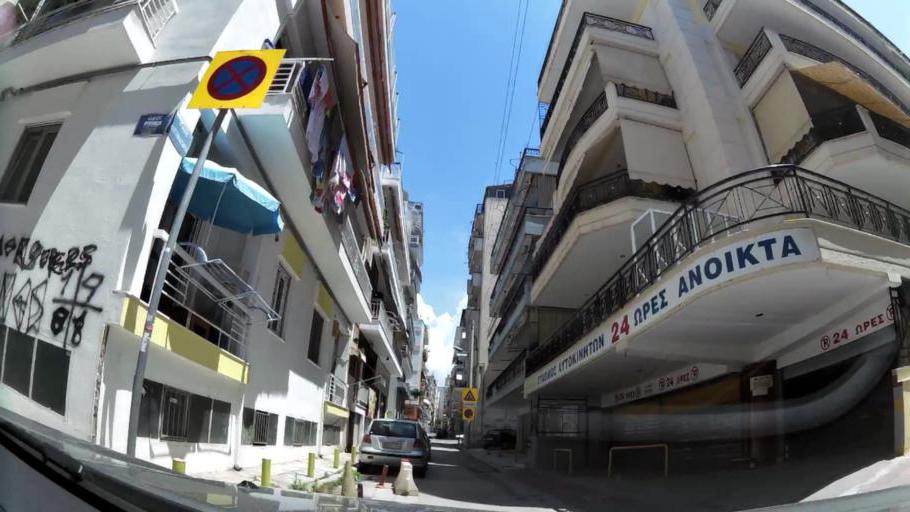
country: GR
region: Central Macedonia
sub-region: Nomos Thessalonikis
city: Triandria
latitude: 40.6064
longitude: 22.9572
